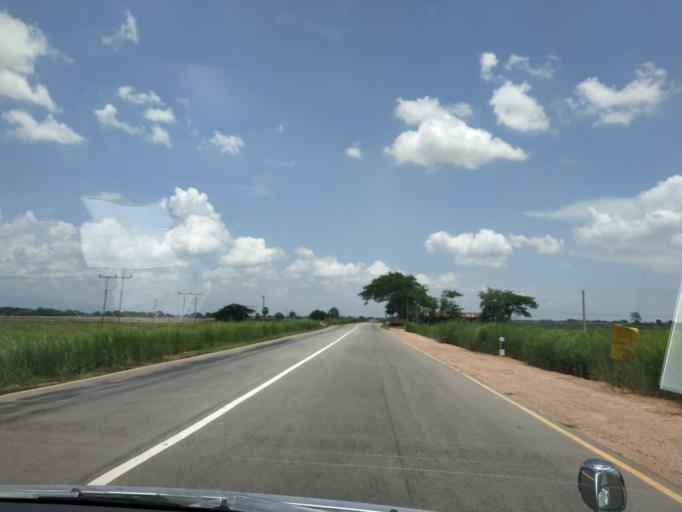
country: MM
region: Mon
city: Kyaikto
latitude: 17.5011
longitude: 96.8068
